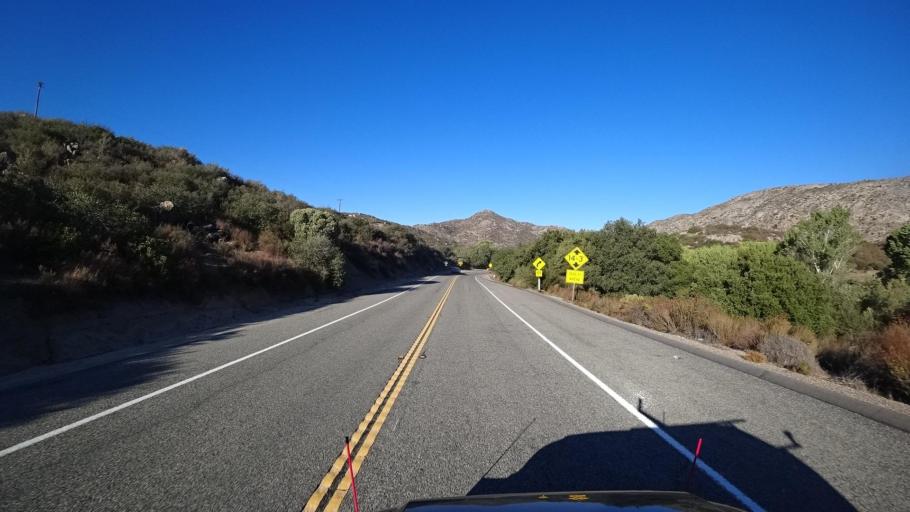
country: MX
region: Baja California
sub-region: Tecate
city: Hacienda Tecate
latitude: 32.5908
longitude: -116.5241
